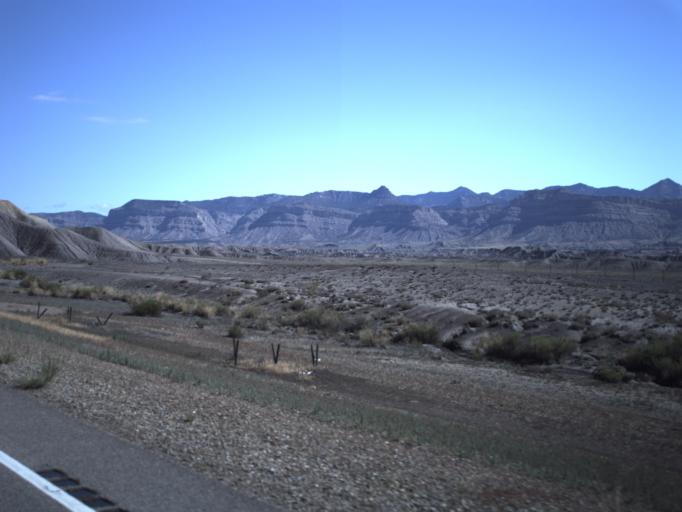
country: US
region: Utah
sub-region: Carbon County
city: East Carbon City
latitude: 39.3378
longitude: -110.3713
